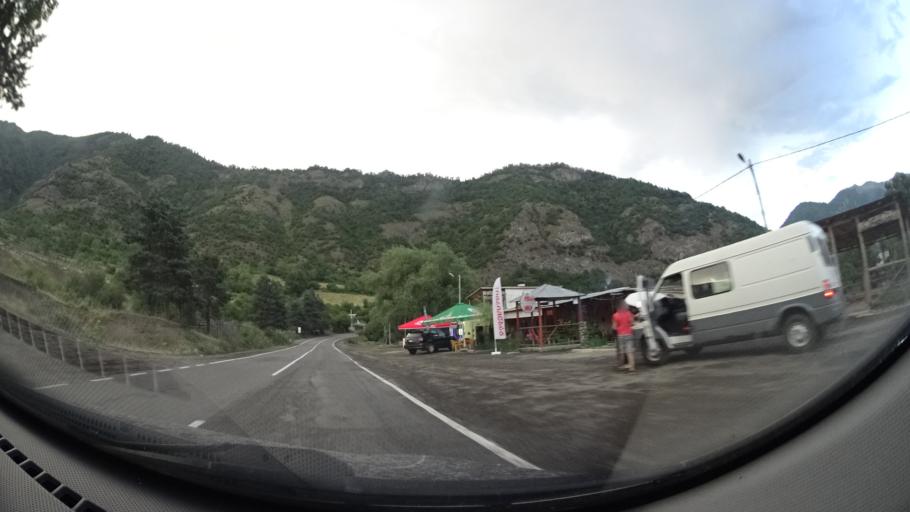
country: GE
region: Samtskhe-Javakheti
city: Borjomi
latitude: 41.8941
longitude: 43.4378
